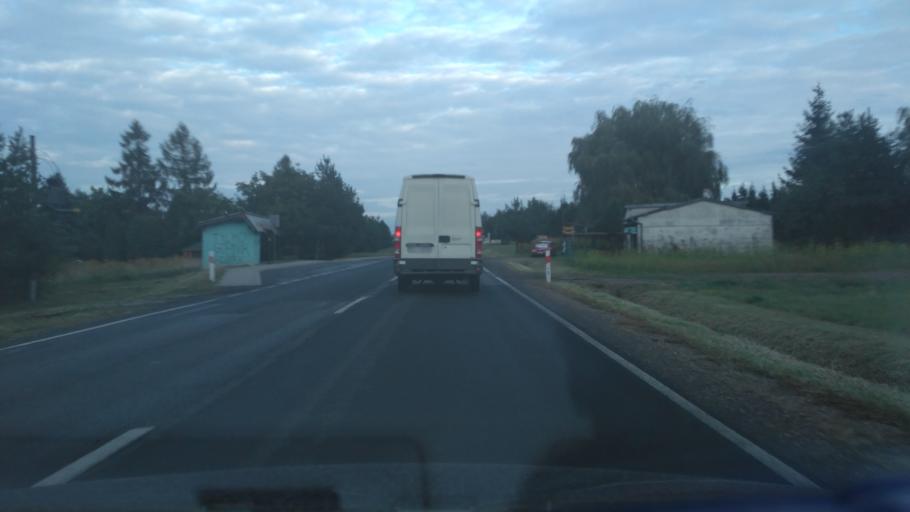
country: PL
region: Lublin Voivodeship
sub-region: Powiat leczynski
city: Spiczyn
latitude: 51.3003
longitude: 22.7576
